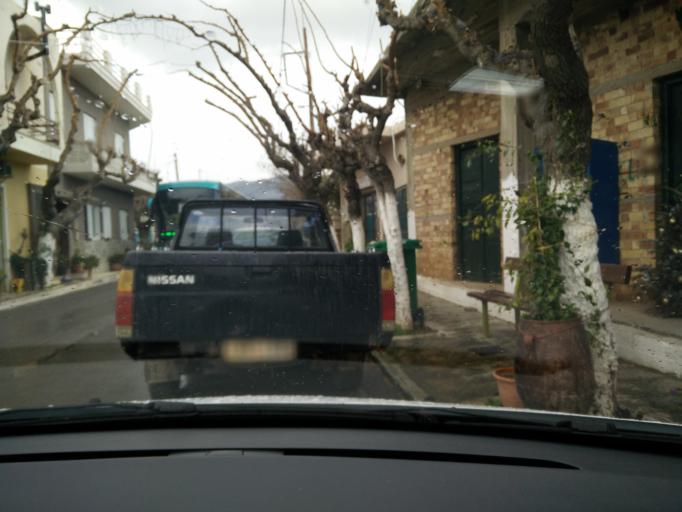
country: GR
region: Crete
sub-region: Nomos Lasithiou
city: Kritsa
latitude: 35.1394
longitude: 25.6596
